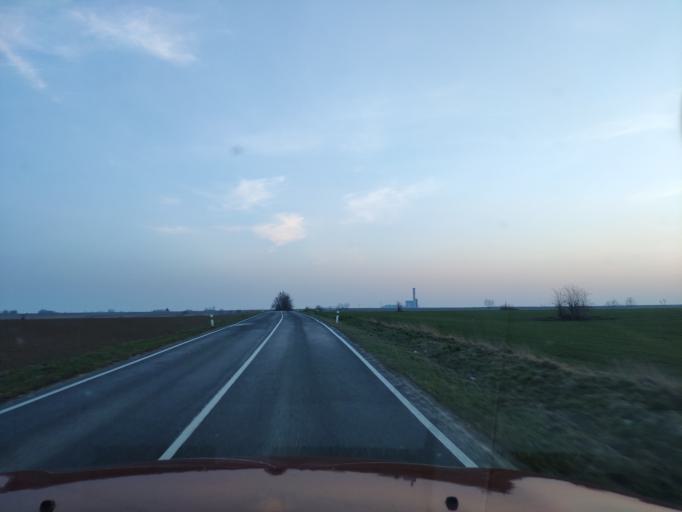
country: SK
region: Trnavsky
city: Leopoldov
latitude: 48.4724
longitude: 17.7058
